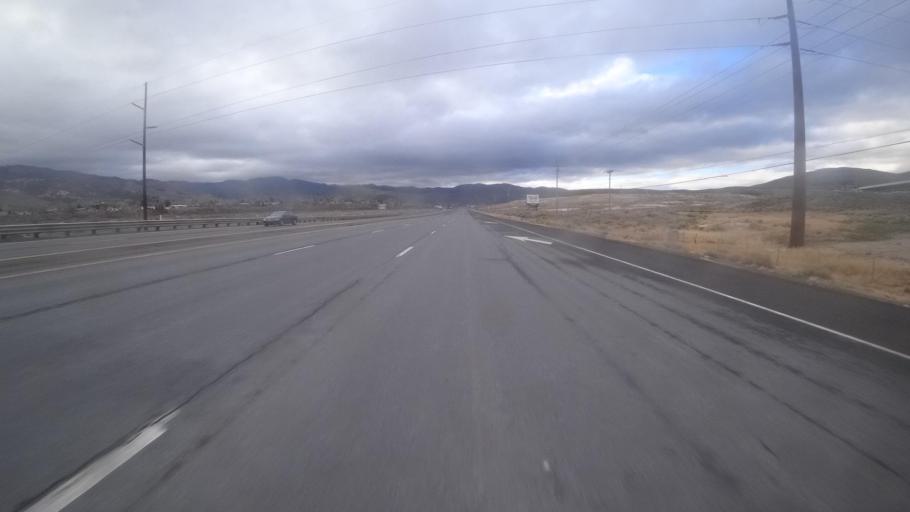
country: US
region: Nevada
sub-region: Storey County
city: Virginia City
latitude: 39.3974
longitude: -119.7433
